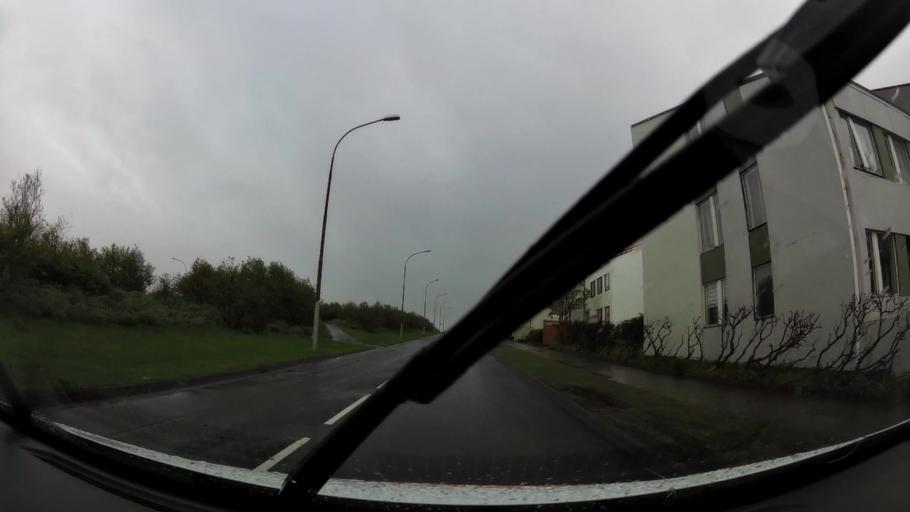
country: IS
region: Capital Region
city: Reykjavik
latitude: 64.1015
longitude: -21.8332
